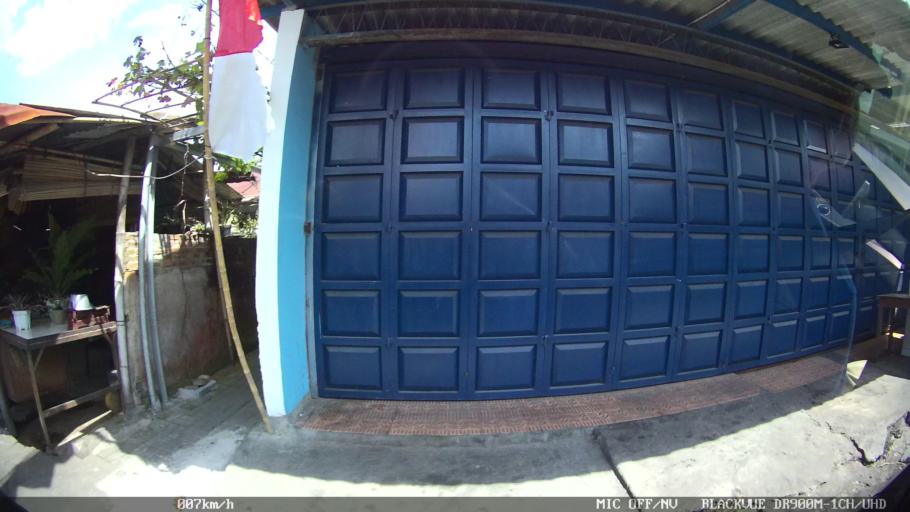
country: ID
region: Daerah Istimewa Yogyakarta
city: Sewon
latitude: -7.8318
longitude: 110.3881
